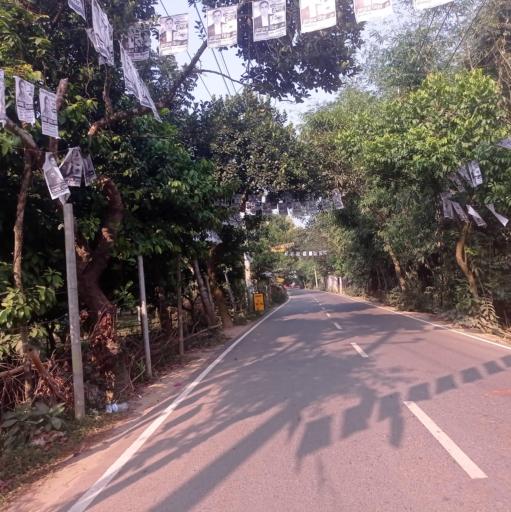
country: BD
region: Dhaka
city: Bhairab Bazar
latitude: 24.0425
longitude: 90.8339
